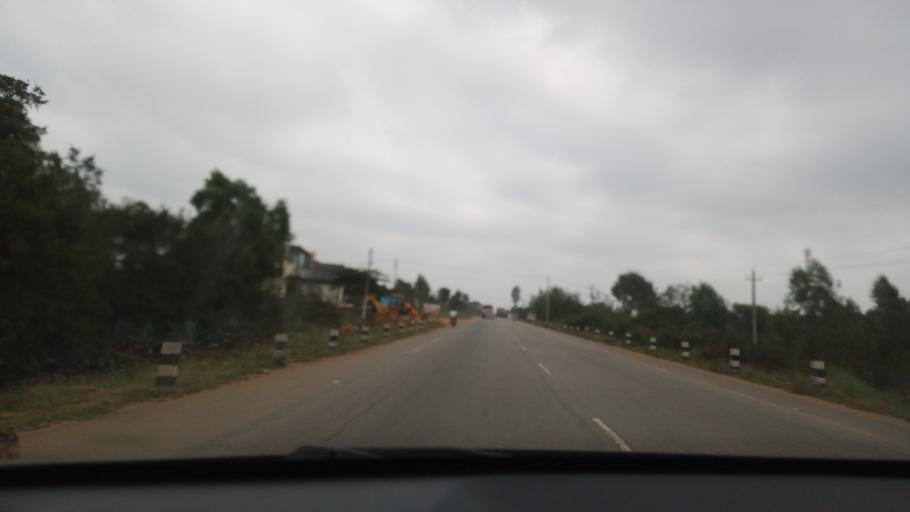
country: IN
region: Karnataka
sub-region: Chikkaballapur
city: Sidlaghatta
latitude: 13.2874
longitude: 77.9613
